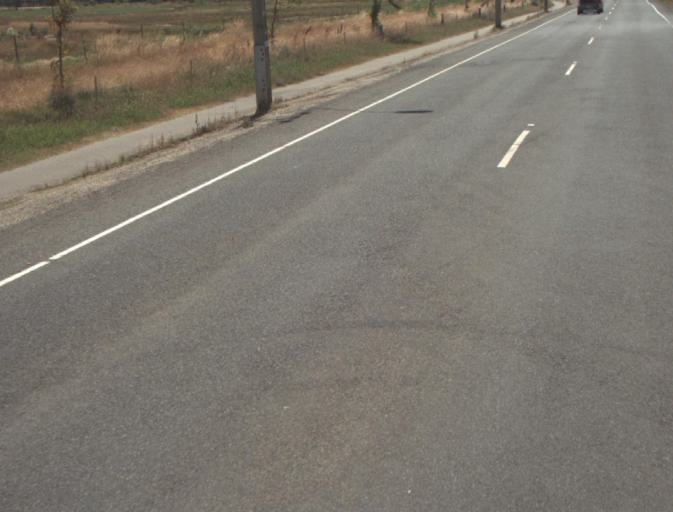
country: AU
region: Tasmania
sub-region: Launceston
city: East Launceston
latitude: -41.4267
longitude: 147.1549
